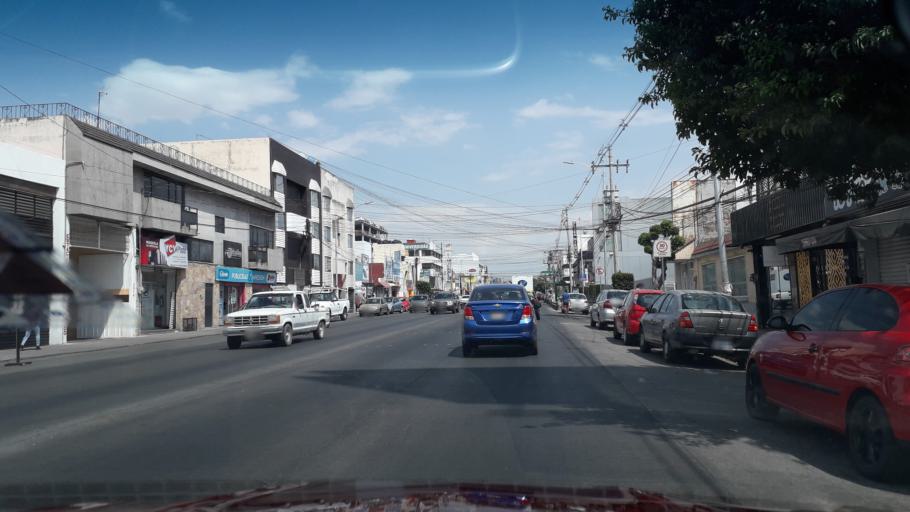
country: MX
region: Puebla
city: Puebla
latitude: 19.0424
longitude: -98.2245
